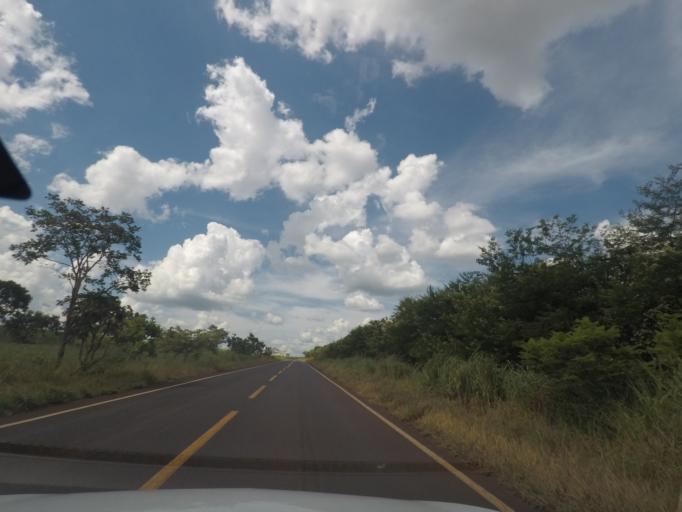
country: BR
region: Minas Gerais
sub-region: Conceicao Das Alagoas
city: Conceicao das Alagoas
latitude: -19.8142
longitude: -48.5864
